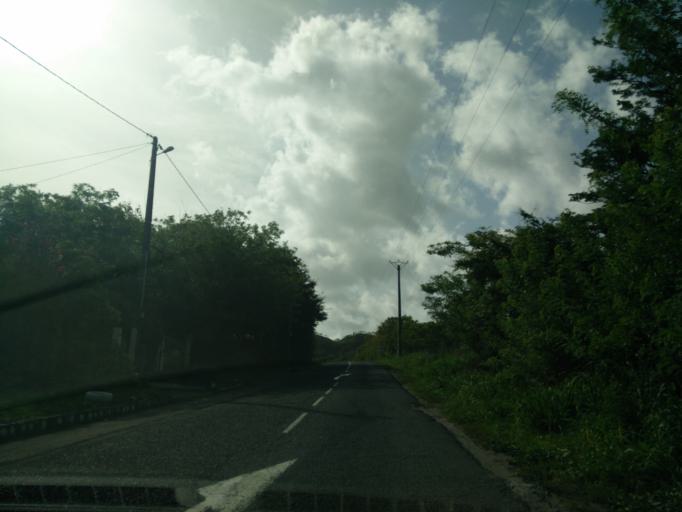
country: MQ
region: Martinique
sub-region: Martinique
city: Saint-Pierre
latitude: 14.7790
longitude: -61.2030
